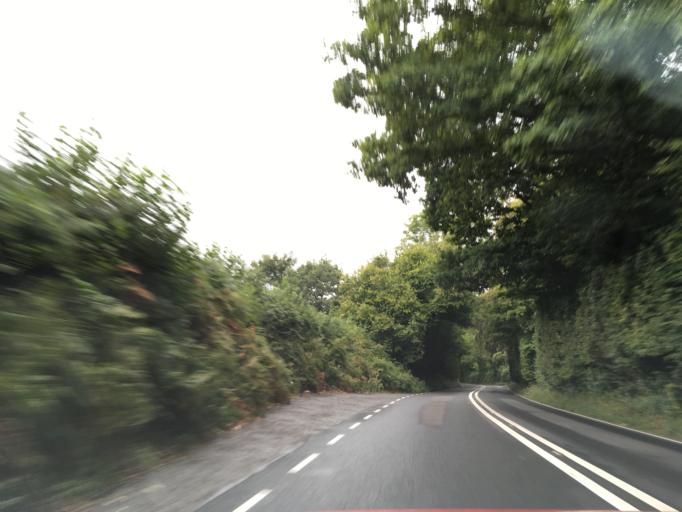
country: GB
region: England
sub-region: Gloucestershire
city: Mitcheldean
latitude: 51.8783
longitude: -2.4462
